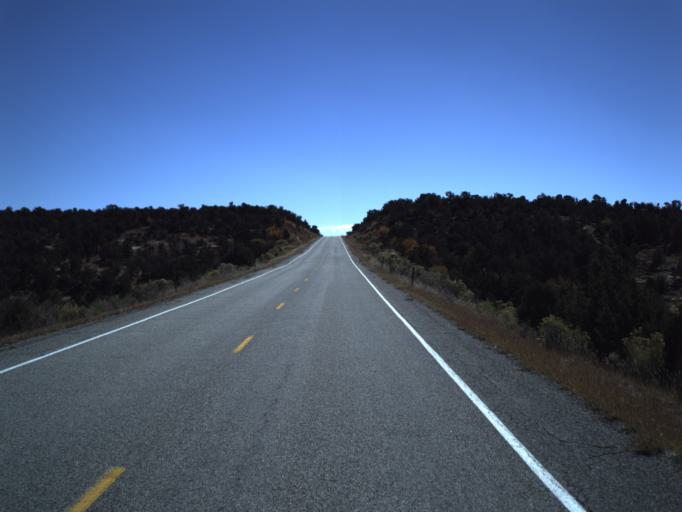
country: US
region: Utah
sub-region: San Juan County
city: Blanding
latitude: 37.5841
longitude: -109.8928
